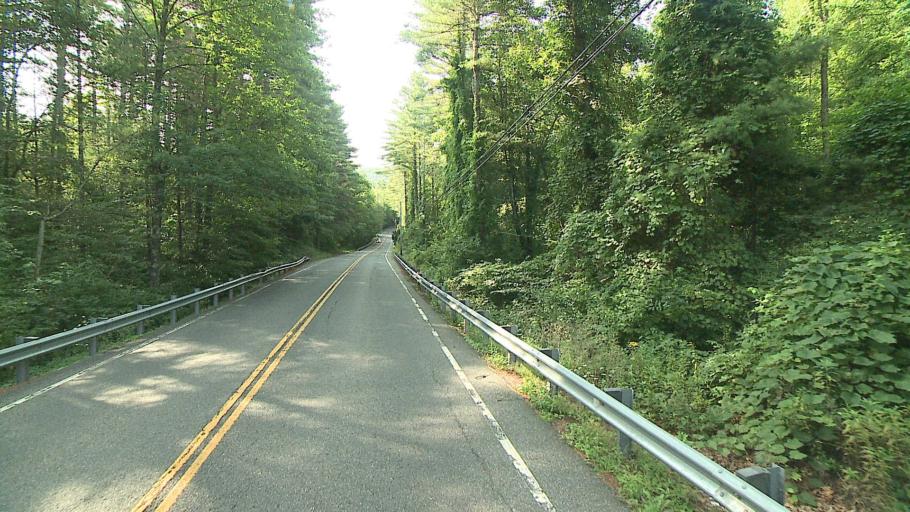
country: US
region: Connecticut
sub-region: Litchfield County
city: Canaan
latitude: 41.8945
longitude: -73.3615
